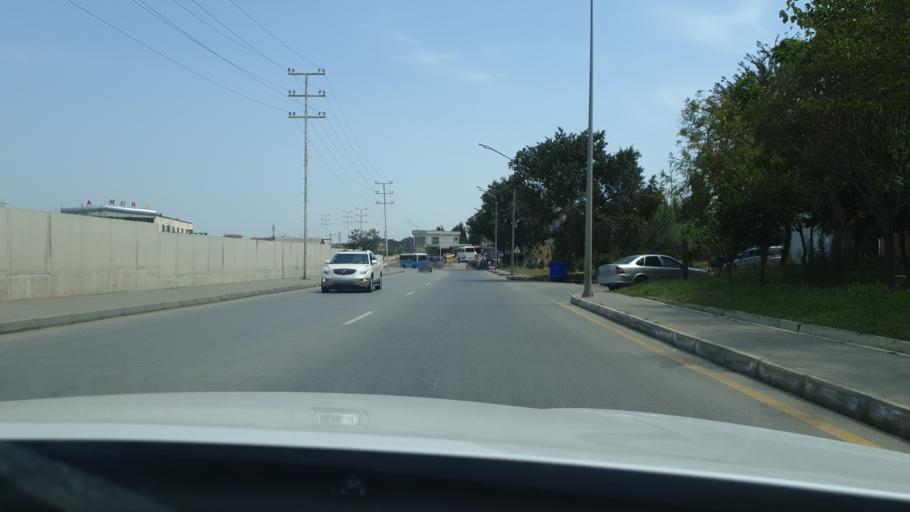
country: AZ
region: Baki
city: Qaracuxur
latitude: 40.3927
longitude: 49.9798
